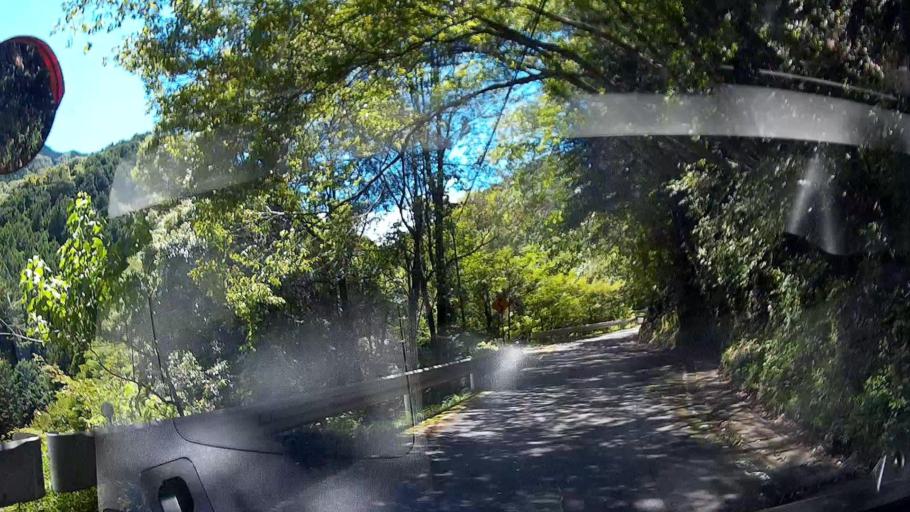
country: JP
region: Shizuoka
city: Shizuoka-shi
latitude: 35.1764
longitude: 138.2876
